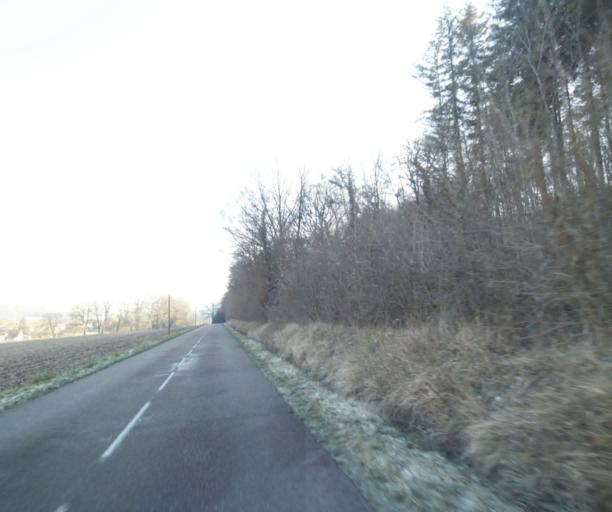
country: FR
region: Champagne-Ardenne
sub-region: Departement de la Haute-Marne
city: Bienville
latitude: 48.5601
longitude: 5.0834
